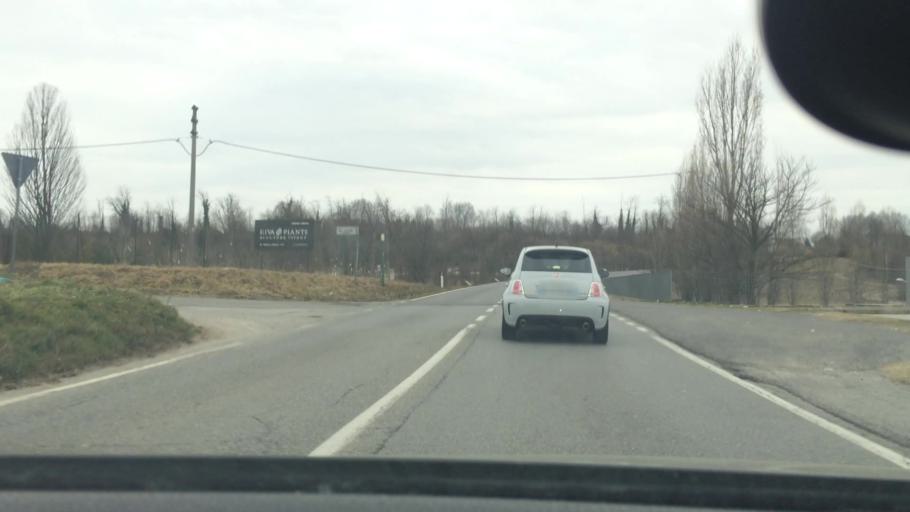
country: IT
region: Lombardy
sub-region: Provincia di Como
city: Lambrugo
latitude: 45.7639
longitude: 9.2286
